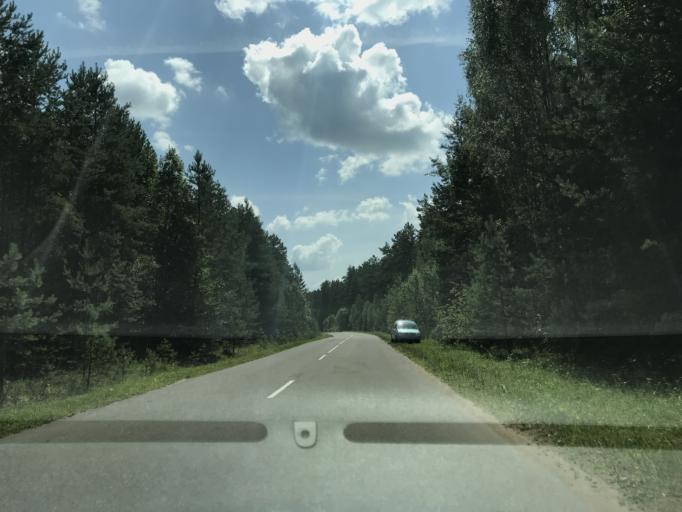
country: BY
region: Minsk
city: Rakaw
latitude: 54.0017
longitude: 26.9853
